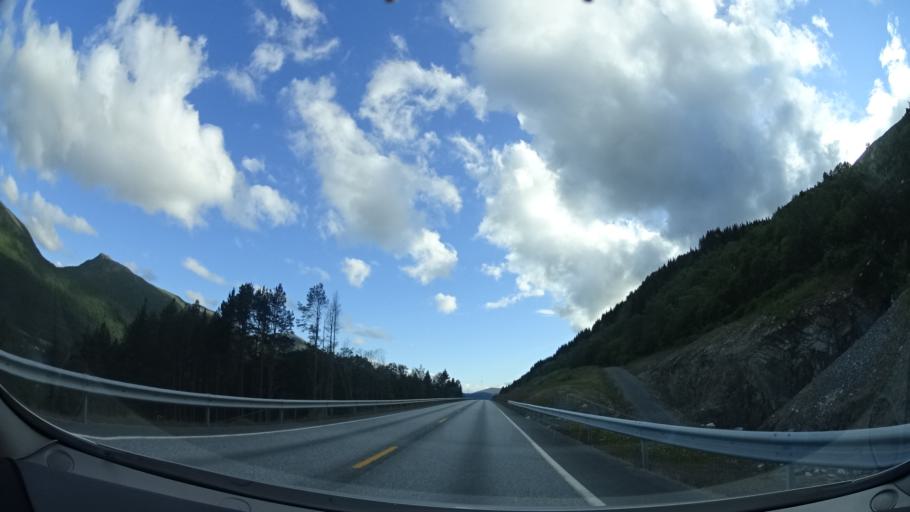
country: NO
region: More og Romsdal
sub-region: Gjemnes
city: Batnfjordsora
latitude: 62.9204
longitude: 7.6986
